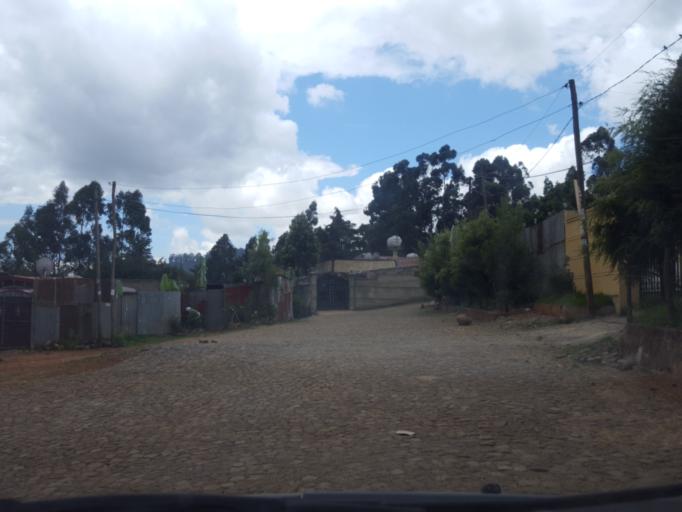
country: ET
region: Adis Abeba
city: Addis Ababa
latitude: 9.0653
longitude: 38.7296
